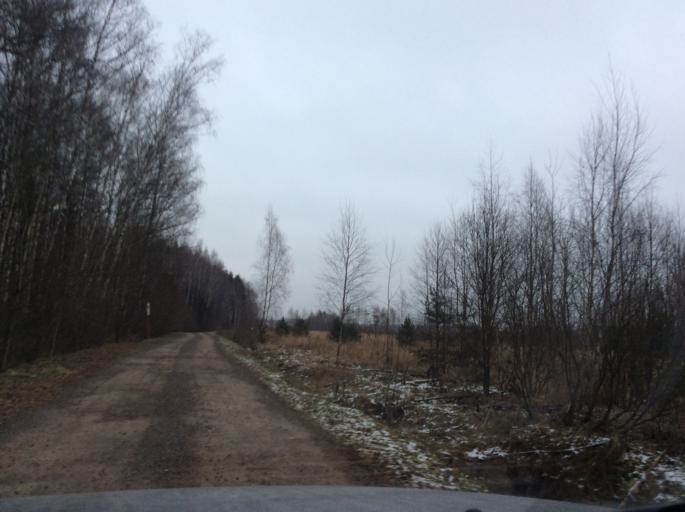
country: RU
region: Moskovskaya
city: Troitsk
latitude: 55.3685
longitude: 37.1700
